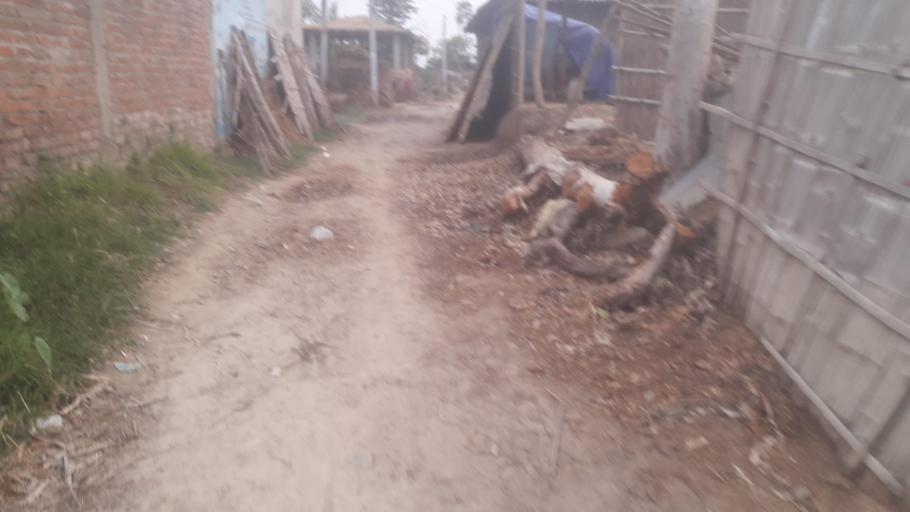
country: NP
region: Eastern Region
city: Siraha
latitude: 26.6562
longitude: 86.1963
